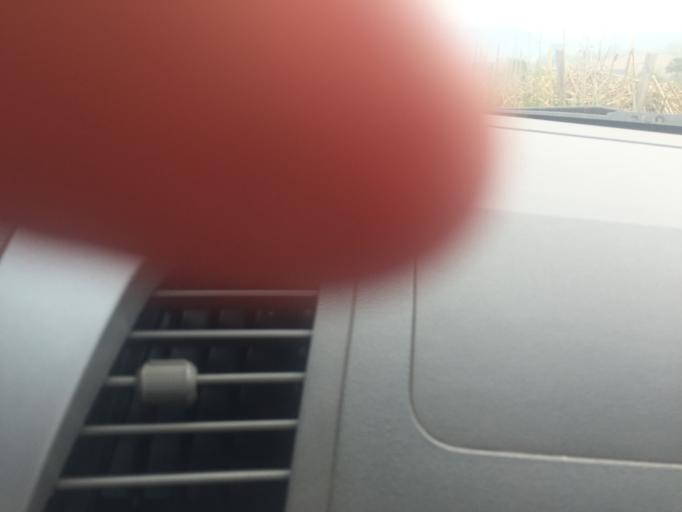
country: LA
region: Vientiane
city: Muang Sanakham
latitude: 18.3786
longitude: 101.5484
